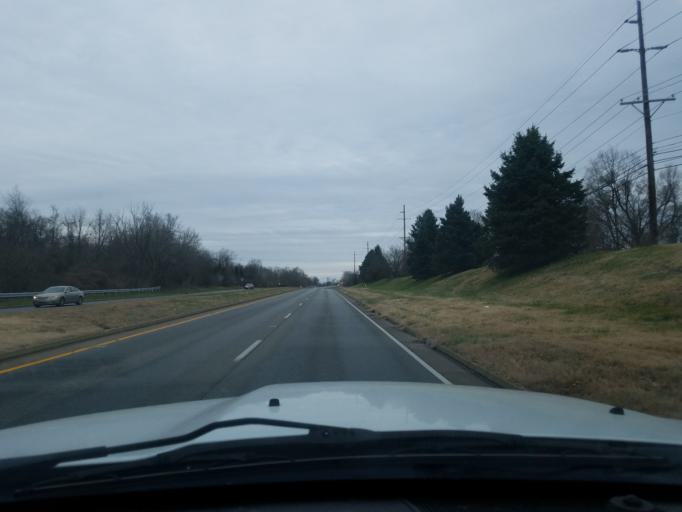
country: US
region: Kentucky
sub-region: Jefferson County
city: Anchorage
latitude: 38.2765
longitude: -85.5647
